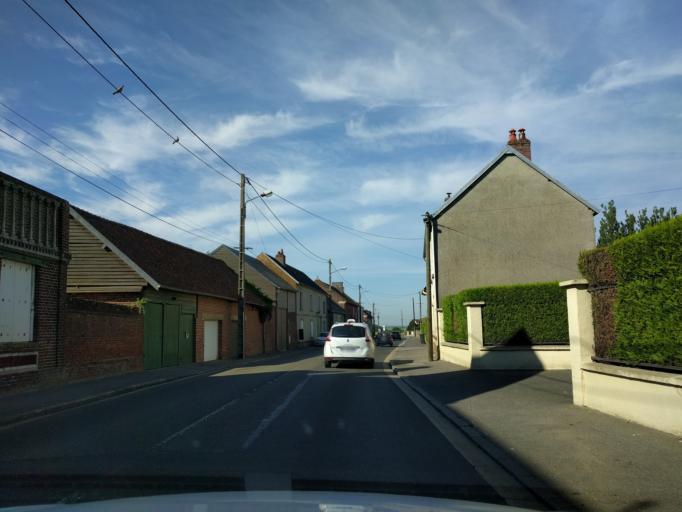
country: FR
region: Picardie
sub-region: Departement de l'Oise
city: Breteuil
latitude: 49.5641
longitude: 2.2182
